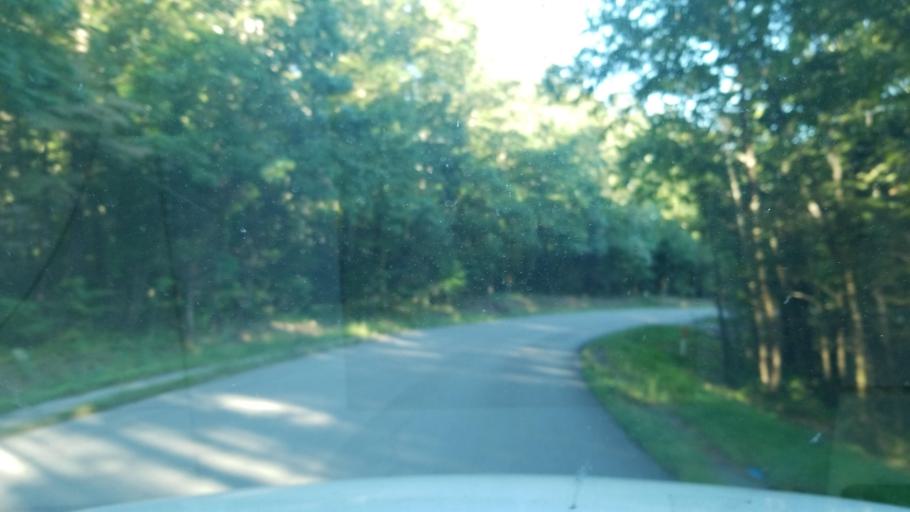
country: US
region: Illinois
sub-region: Hardin County
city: Elizabethtown
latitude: 37.5983
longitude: -88.3647
